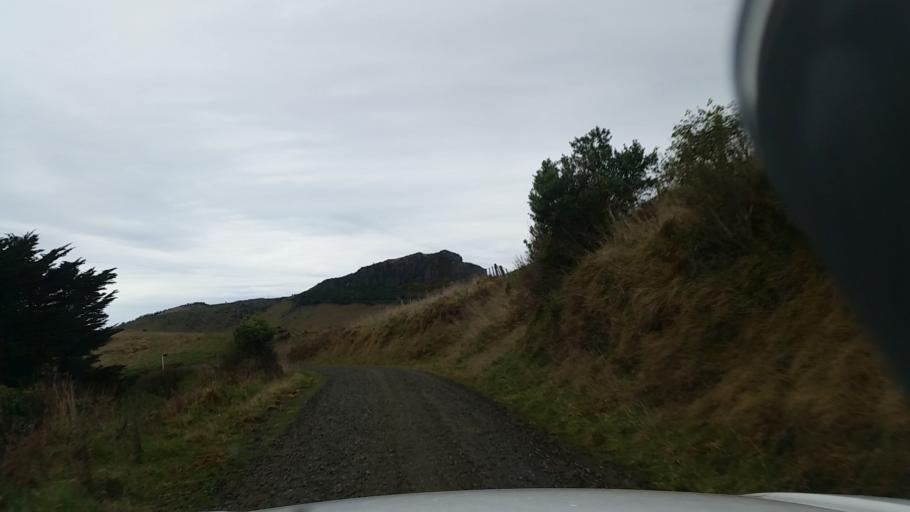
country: NZ
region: Canterbury
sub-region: Christchurch City
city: Christchurch
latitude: -43.7377
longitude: 173.0294
